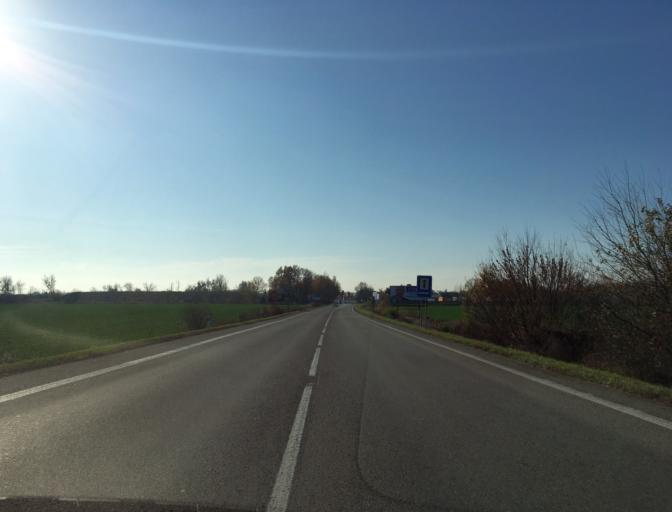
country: SK
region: Nitriansky
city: Komarno
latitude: 47.7738
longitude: 18.1583
